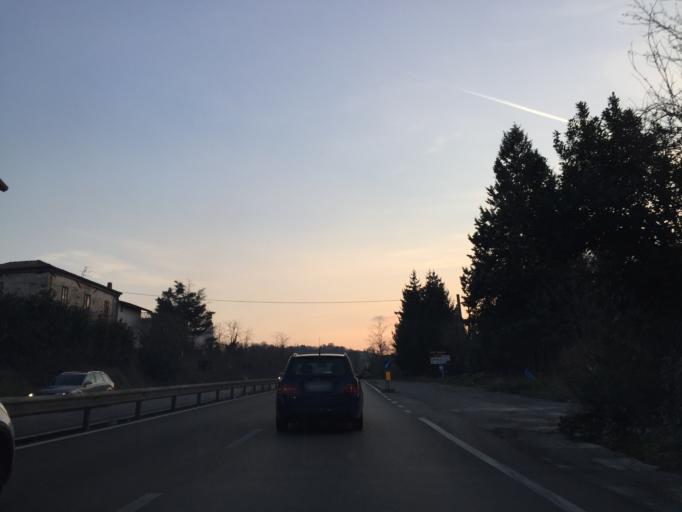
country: IT
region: Campania
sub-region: Provincia di Avellino
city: Atripalda
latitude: 40.9152
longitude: 14.8244
